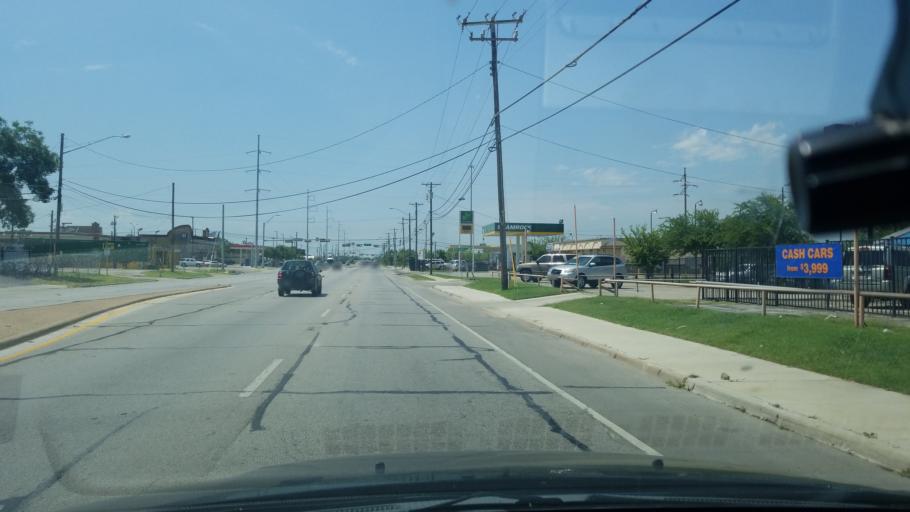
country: US
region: Texas
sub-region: Dallas County
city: Balch Springs
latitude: 32.7212
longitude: -96.6831
